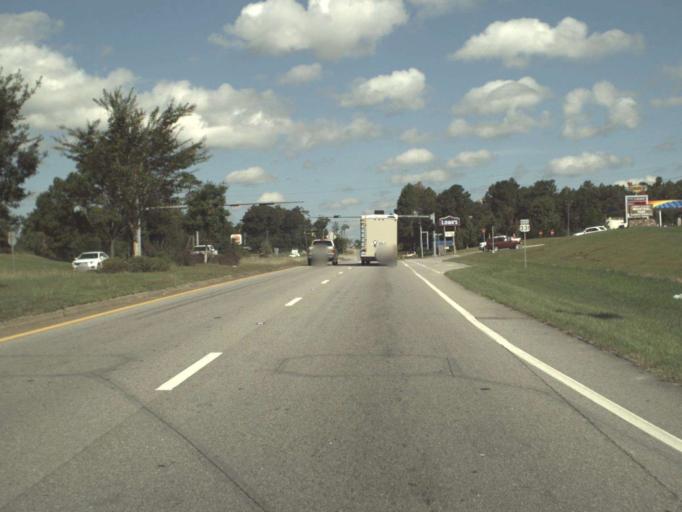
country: US
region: Florida
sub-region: Walton County
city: DeFuniak Springs
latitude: 30.6954
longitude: -86.1224
